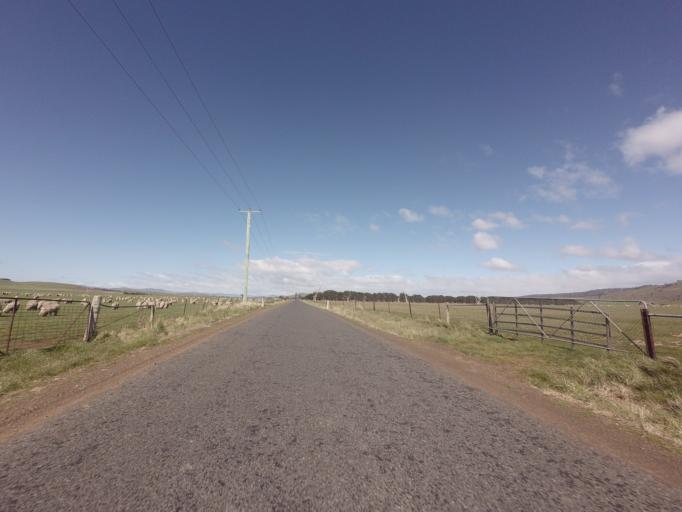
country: AU
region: Tasmania
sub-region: Northern Midlands
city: Evandale
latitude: -41.9903
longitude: 147.4523
